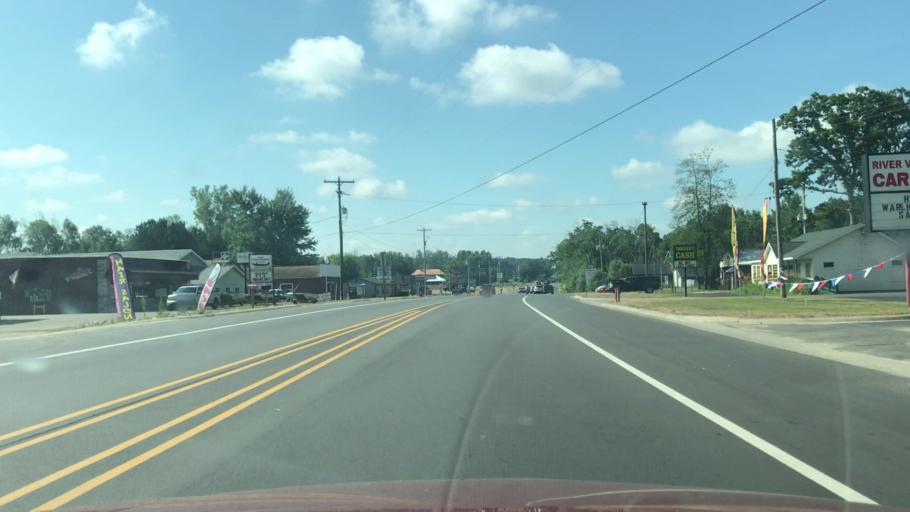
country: US
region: Michigan
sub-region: Newaygo County
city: Newaygo
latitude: 43.4024
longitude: -85.8008
